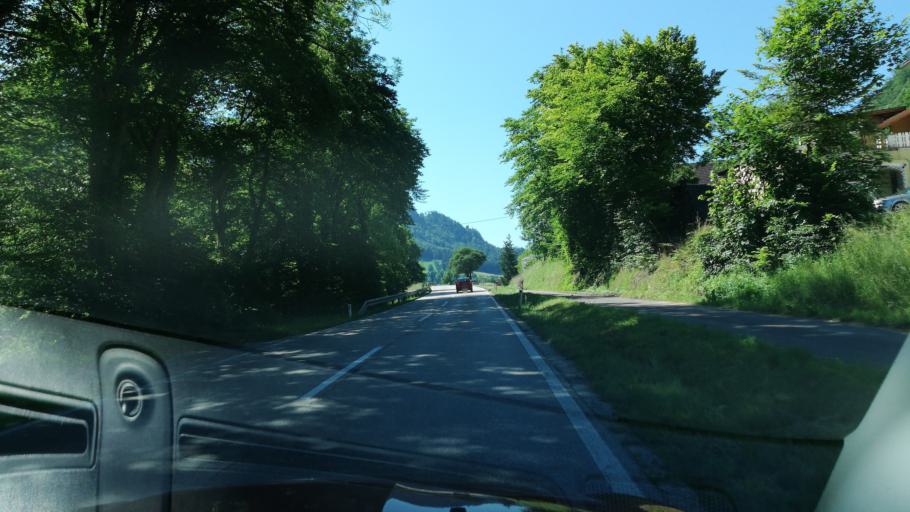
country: AT
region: Upper Austria
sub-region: Politischer Bezirk Kirchdorf an der Krems
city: Gruenburg
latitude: 47.9307
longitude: 14.2471
